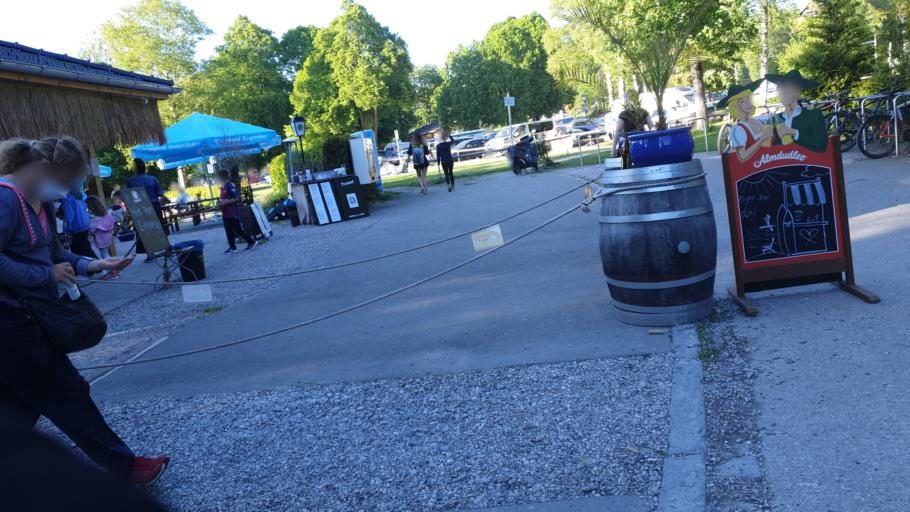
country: DE
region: Bavaria
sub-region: Upper Bavaria
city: Seehausen am Staffelsee
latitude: 47.6791
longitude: 11.1877
